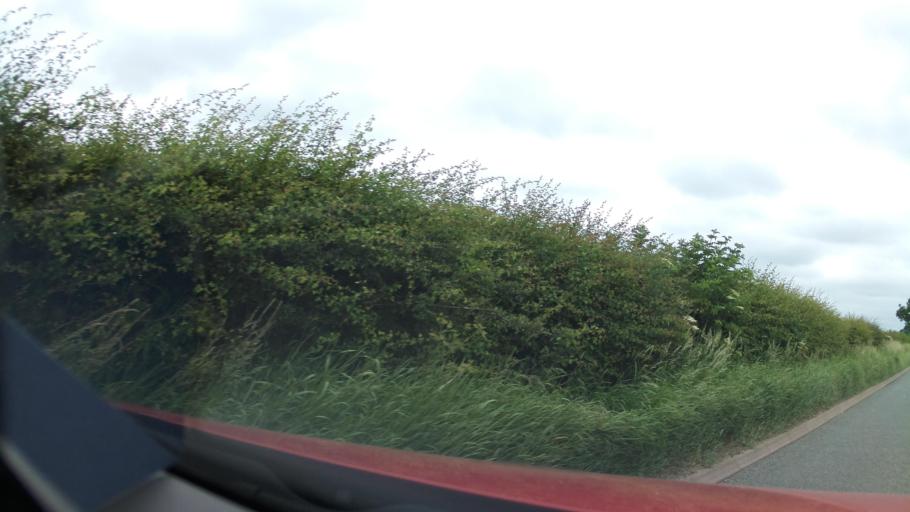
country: GB
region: England
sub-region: Leicestershire
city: Asfordby
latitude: 52.7671
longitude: -0.9670
